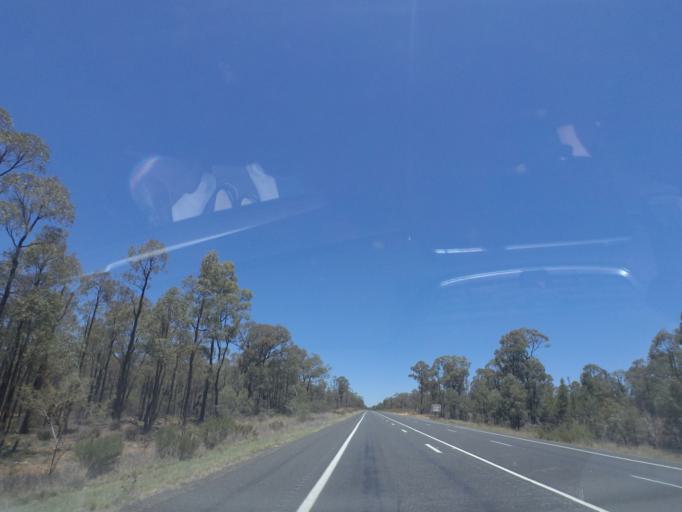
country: AU
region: New South Wales
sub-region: Warrumbungle Shire
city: Coonabarabran
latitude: -30.8700
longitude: 149.4506
